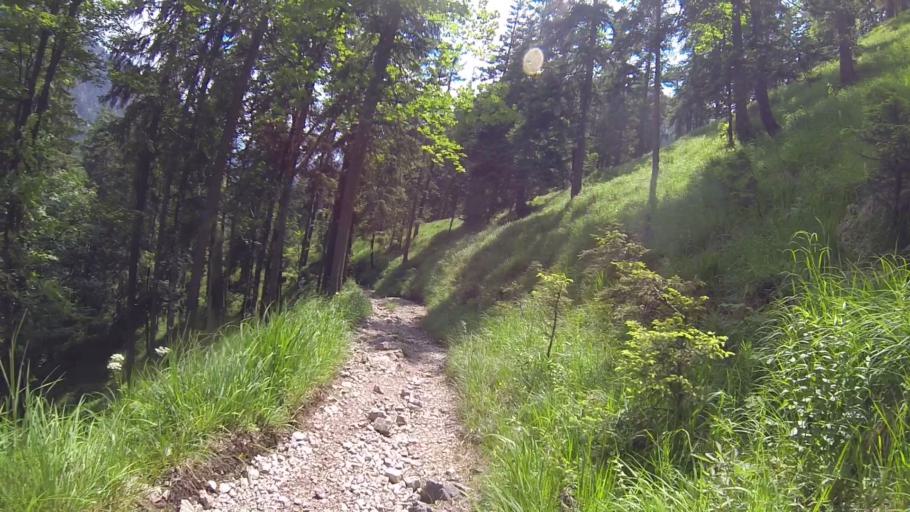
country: DE
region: Bavaria
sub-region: Swabia
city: Halblech
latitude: 47.5268
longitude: 10.8377
